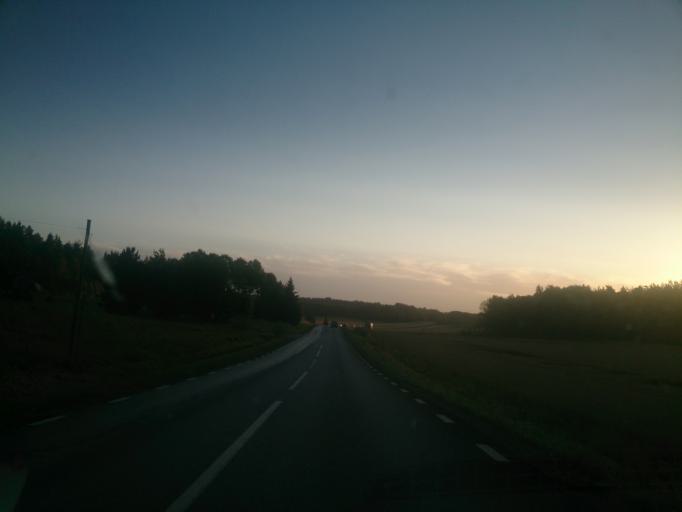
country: SE
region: Soedermanland
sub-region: Nykopings Kommun
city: Nykoping
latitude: 58.7775
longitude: 17.0481
